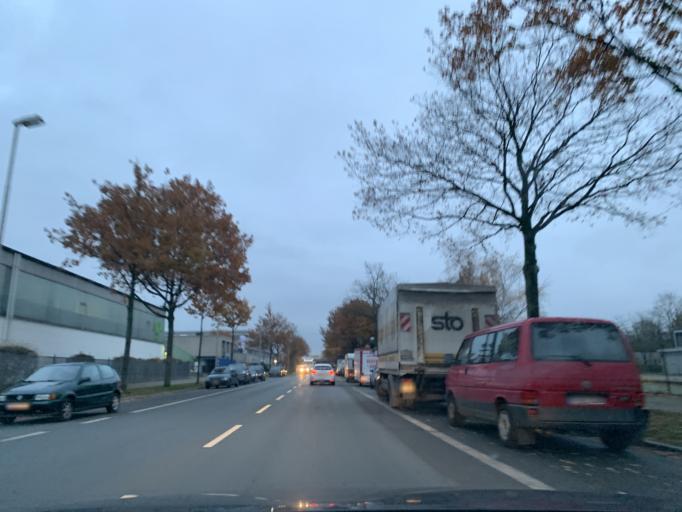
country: DE
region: Bremen
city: Bremen
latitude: 53.1060
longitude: 8.7971
